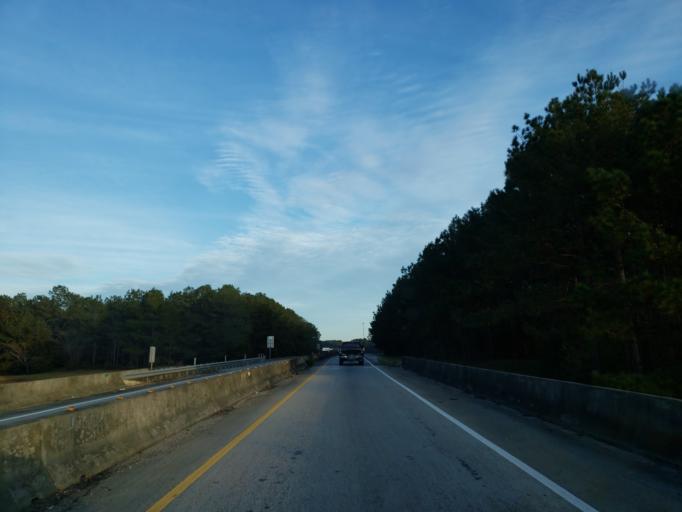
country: US
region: Mississippi
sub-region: Forrest County
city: Hattiesburg
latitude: 31.2399
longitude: -89.3234
